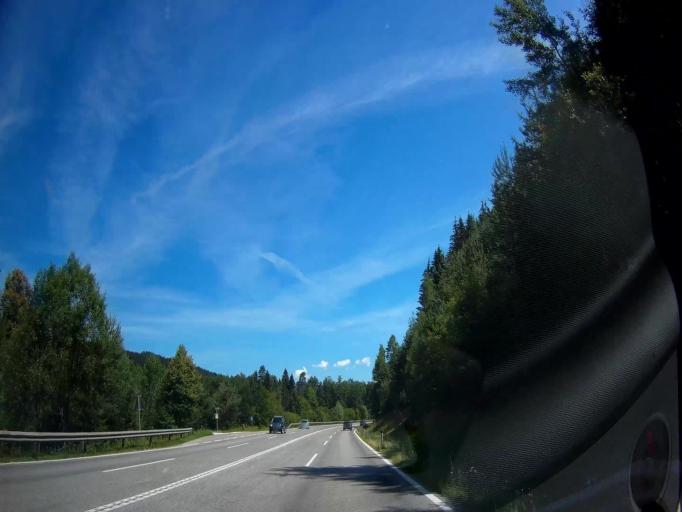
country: AT
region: Carinthia
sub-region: Politischer Bezirk Sankt Veit an der Glan
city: Molbling
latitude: 46.8166
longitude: 14.4315
